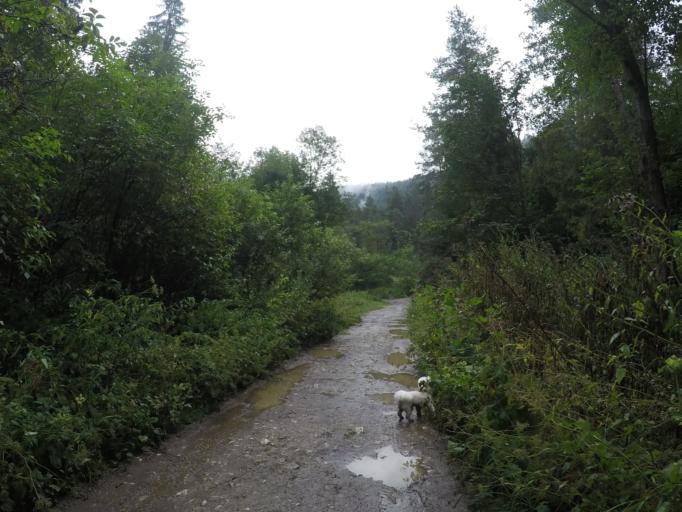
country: SK
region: Kosicky
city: Spisska Nova Ves
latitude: 48.9554
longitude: 20.4408
